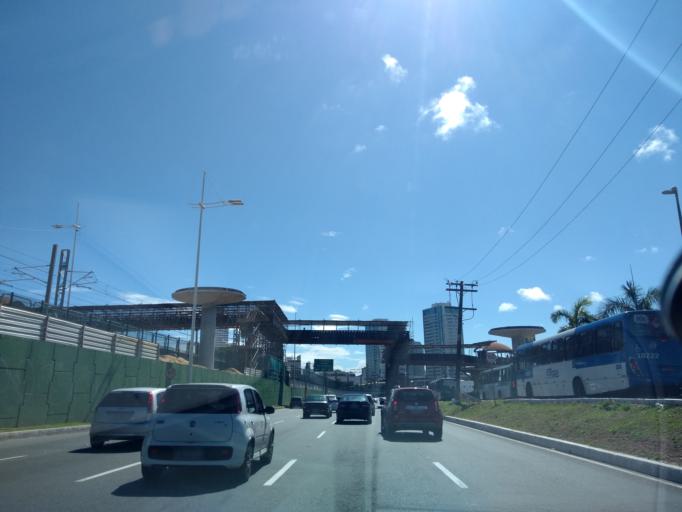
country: BR
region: Bahia
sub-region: Salvador
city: Salvador
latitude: -12.9746
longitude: -38.4520
